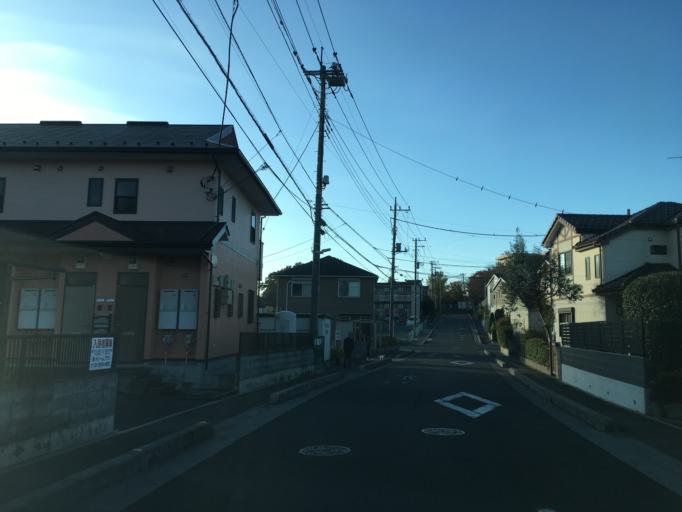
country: JP
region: Saitama
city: Tokorozawa
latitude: 35.7857
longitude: 139.4321
